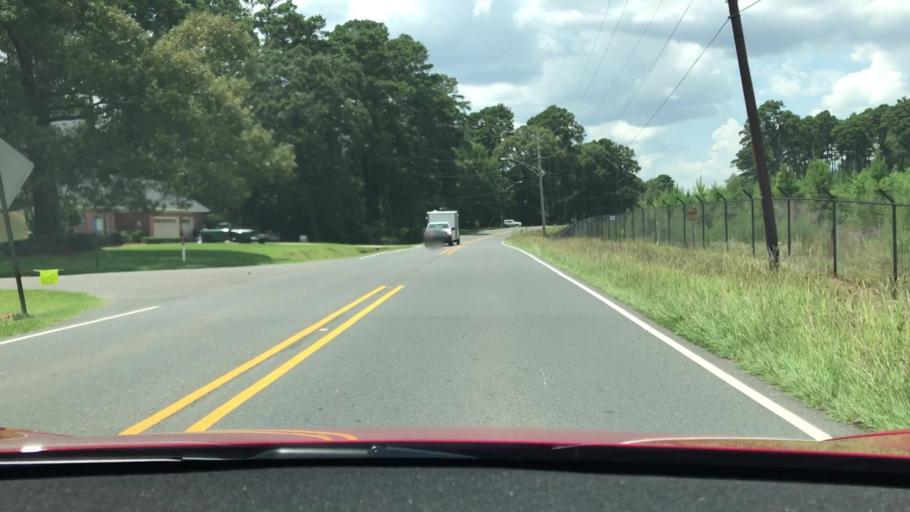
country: US
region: Louisiana
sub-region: Bossier Parish
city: Bossier City
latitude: 32.3847
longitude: -93.7153
